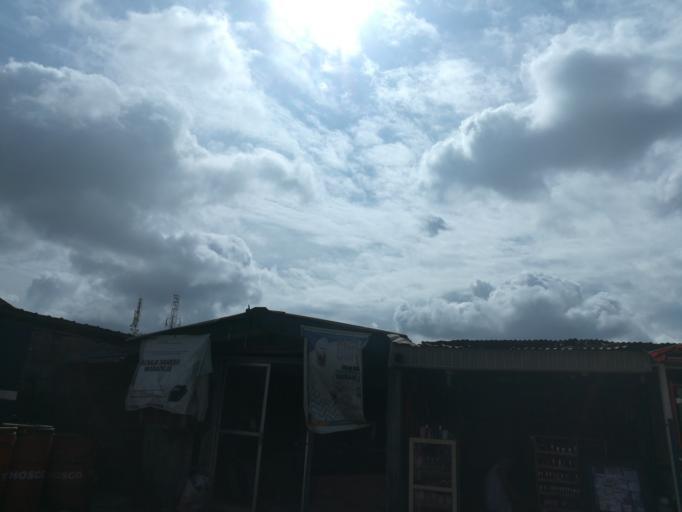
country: NG
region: Lagos
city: Somolu
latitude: 6.5455
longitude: 3.3740
